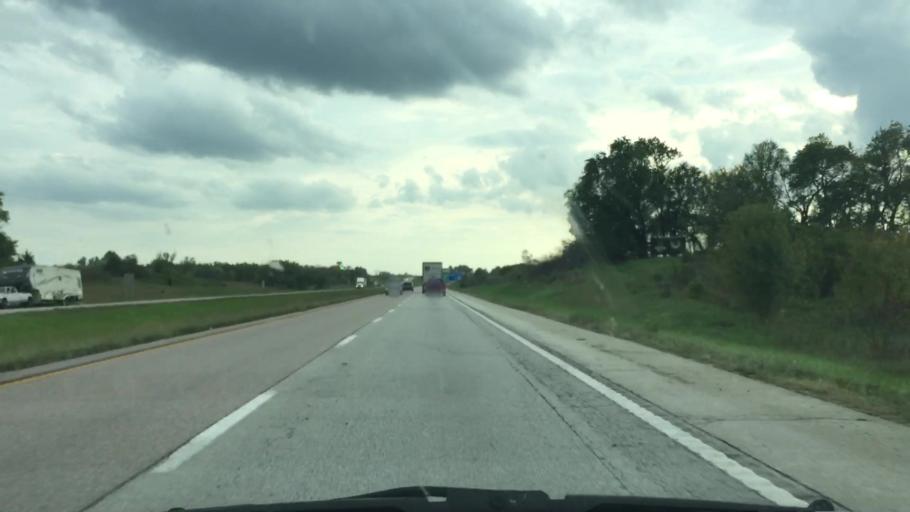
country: US
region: Missouri
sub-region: Clinton County
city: Lathrop
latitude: 39.5617
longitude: -94.2660
